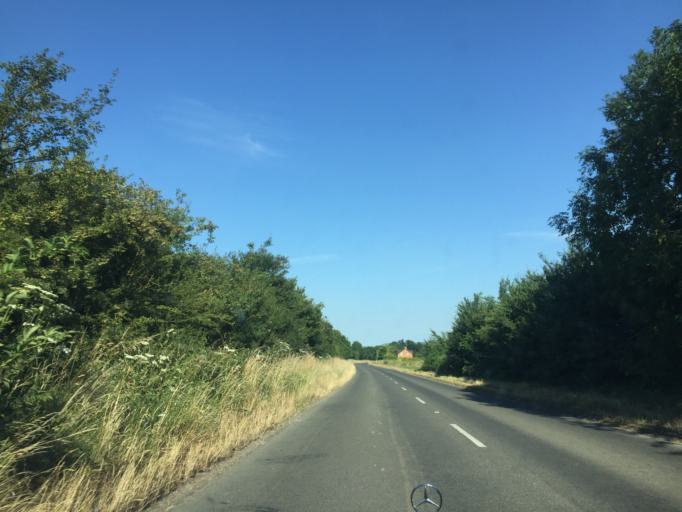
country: GB
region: England
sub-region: Buckinghamshire
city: Long Crendon
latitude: 51.7225
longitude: -1.0406
